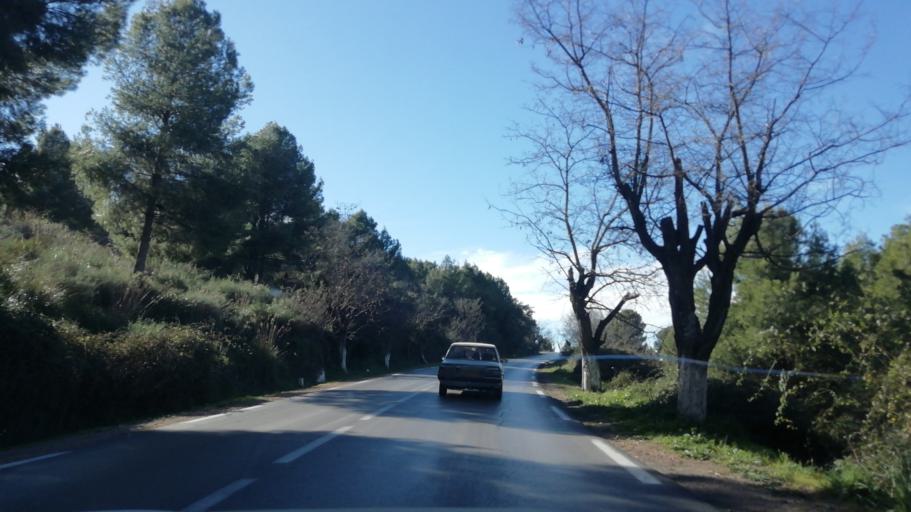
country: DZ
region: Tlemcen
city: Mansoura
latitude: 34.8503
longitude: -1.3537
